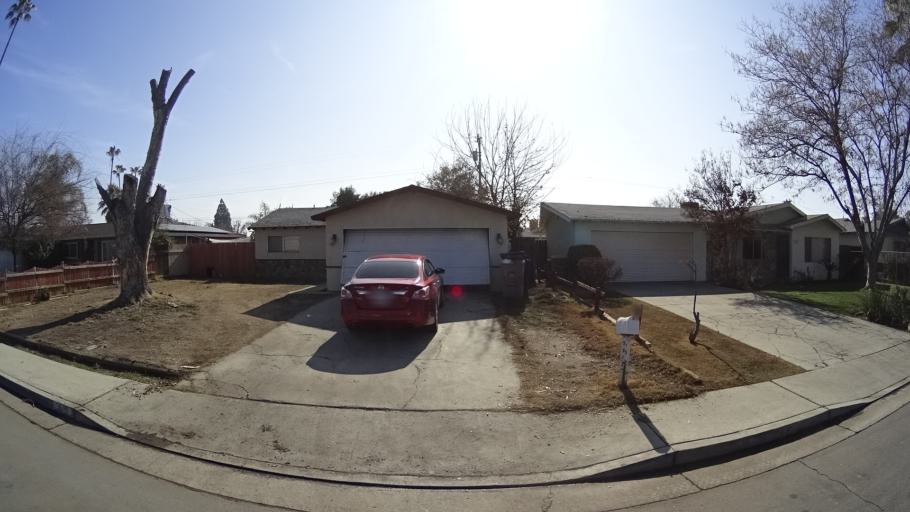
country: US
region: California
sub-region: Kern County
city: Bakersfield
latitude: 35.3355
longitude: -119.0471
